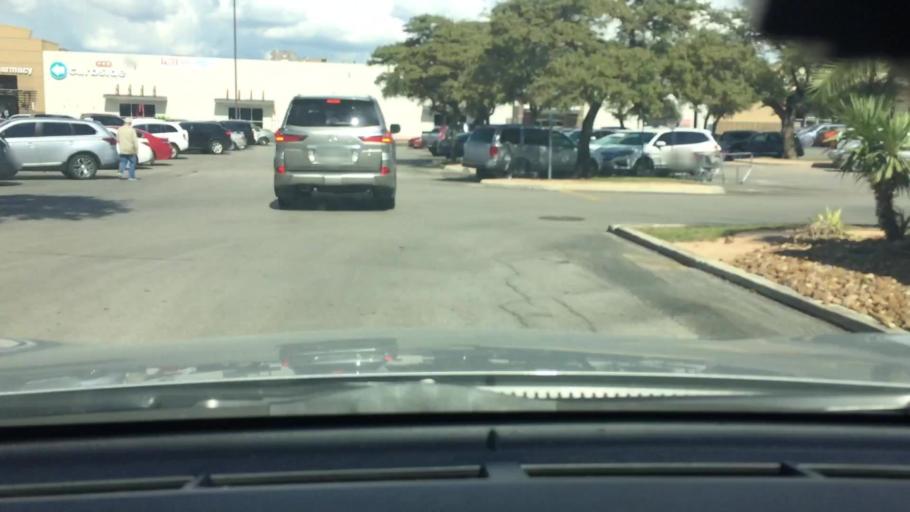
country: US
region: Texas
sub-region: Bexar County
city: Shavano Park
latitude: 29.5617
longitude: -98.5894
